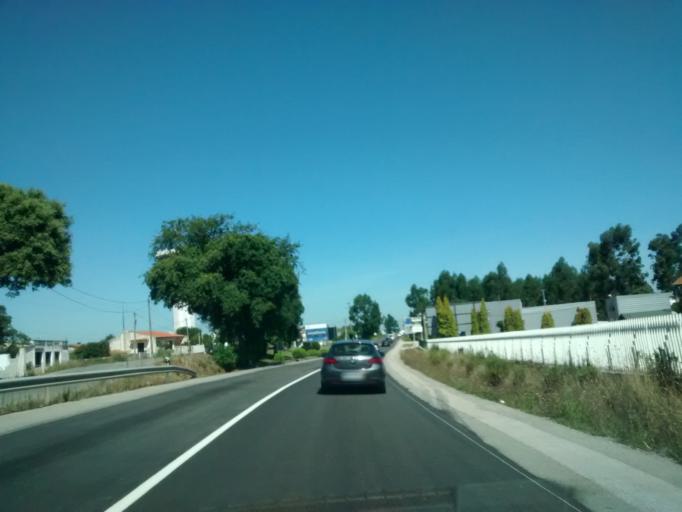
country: PT
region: Aveiro
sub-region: Oliveira do Bairro
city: Oia
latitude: 40.5398
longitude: -8.5298
